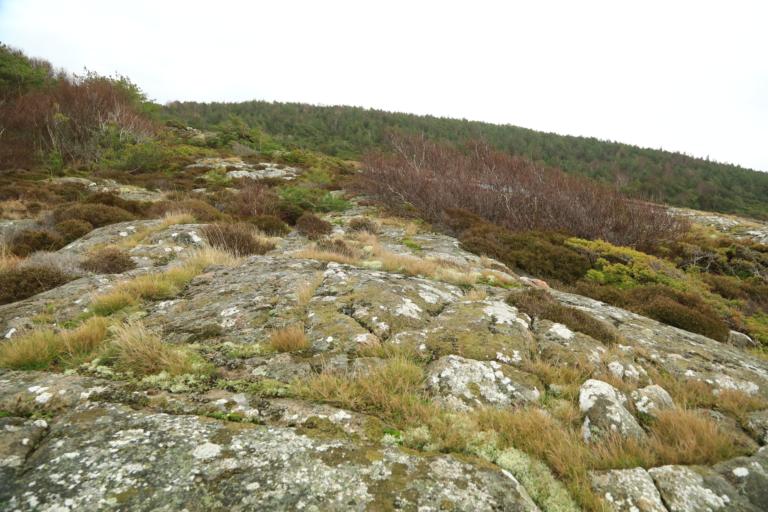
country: SE
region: Halland
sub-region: Varbergs Kommun
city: Varberg
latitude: 57.1779
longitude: 12.2025
